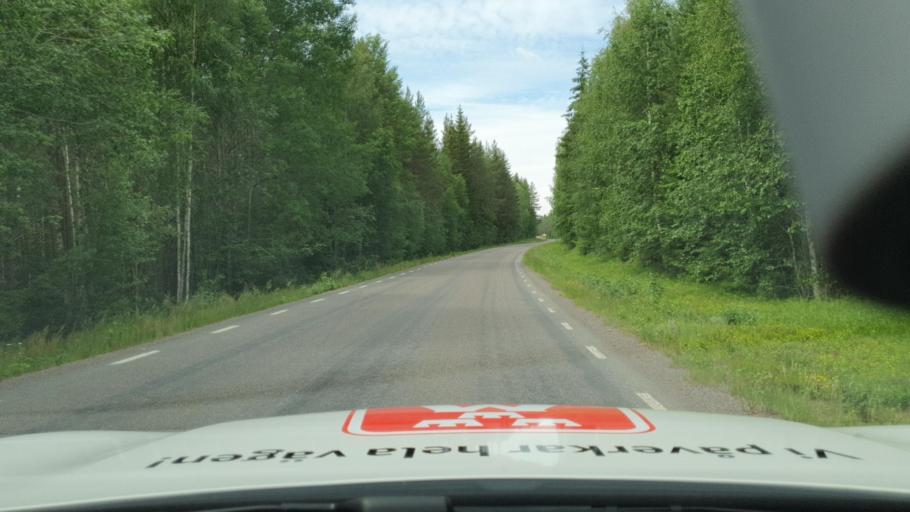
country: NO
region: Hedmark
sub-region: Grue
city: Kirkenaer
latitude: 60.6919
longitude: 12.6269
